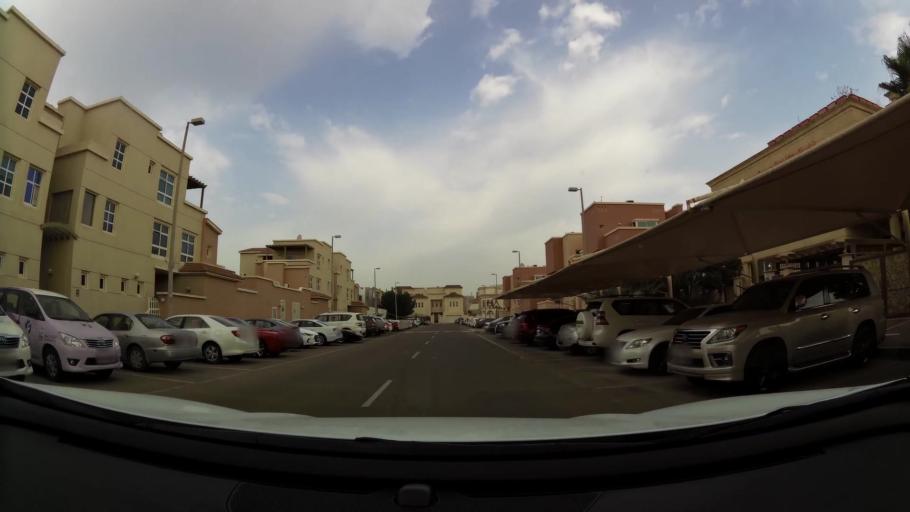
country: AE
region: Abu Dhabi
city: Abu Dhabi
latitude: 24.4747
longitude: 54.3853
